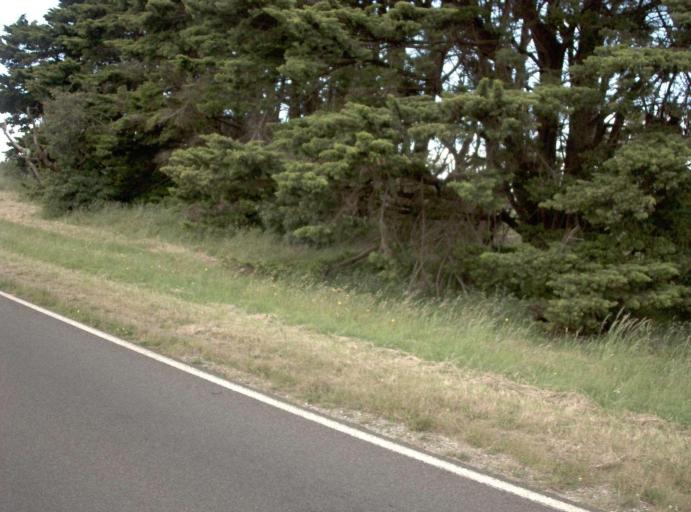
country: AU
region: Victoria
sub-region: Baw Baw
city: Warragul
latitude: -38.1288
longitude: 145.9291
